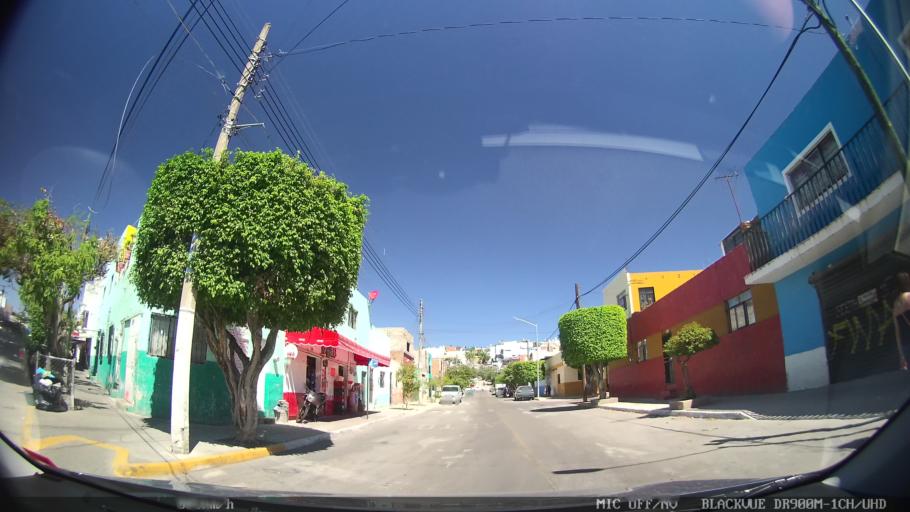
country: MX
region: Jalisco
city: Tlaquepaque
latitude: 20.6881
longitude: -103.2850
